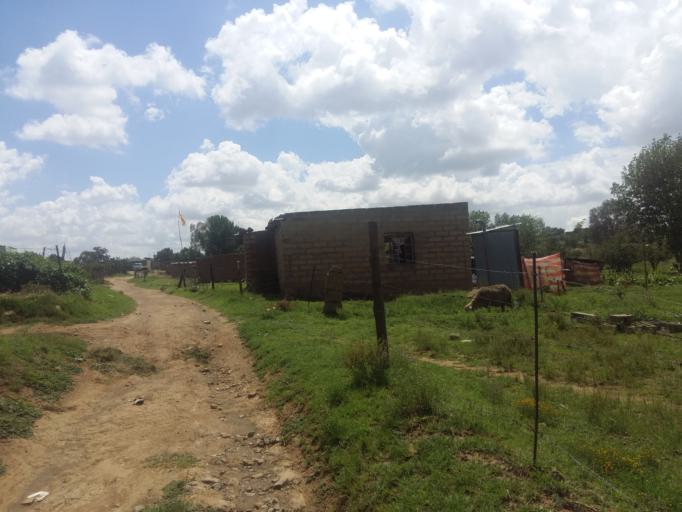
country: LS
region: Mafeteng
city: Mafeteng
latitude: -29.7592
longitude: 27.1119
